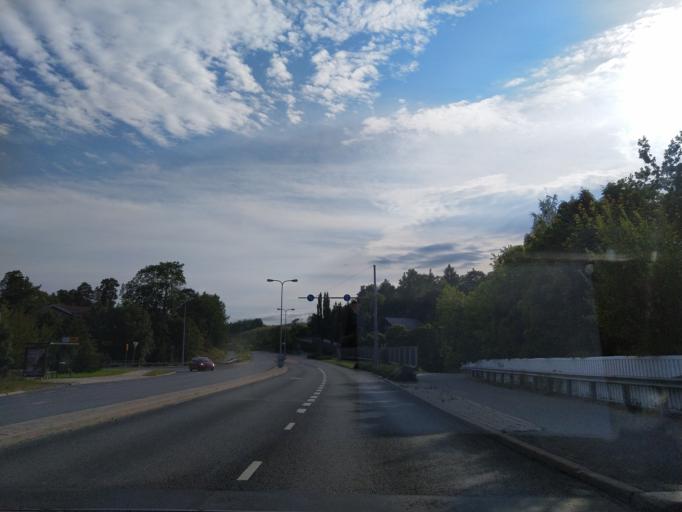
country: FI
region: Varsinais-Suomi
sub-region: Turku
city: Turku
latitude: 60.4216
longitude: 22.2341
